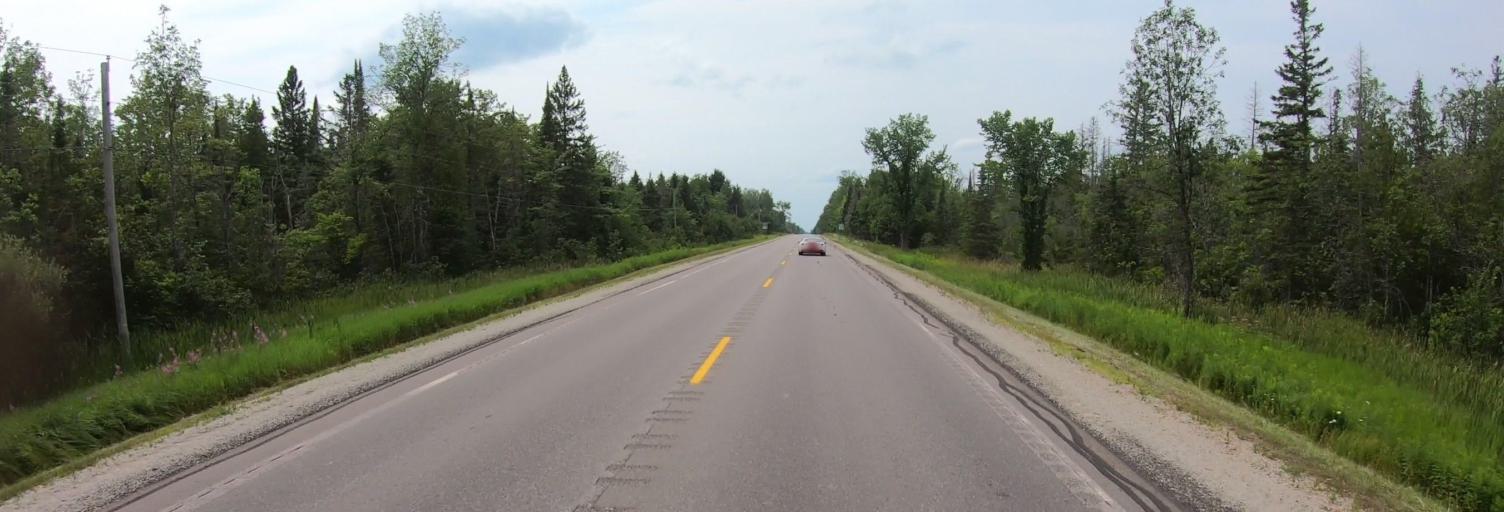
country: US
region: Michigan
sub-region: Marquette County
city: K. I. Sawyer Air Force Base
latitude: 46.3476
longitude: -87.1694
